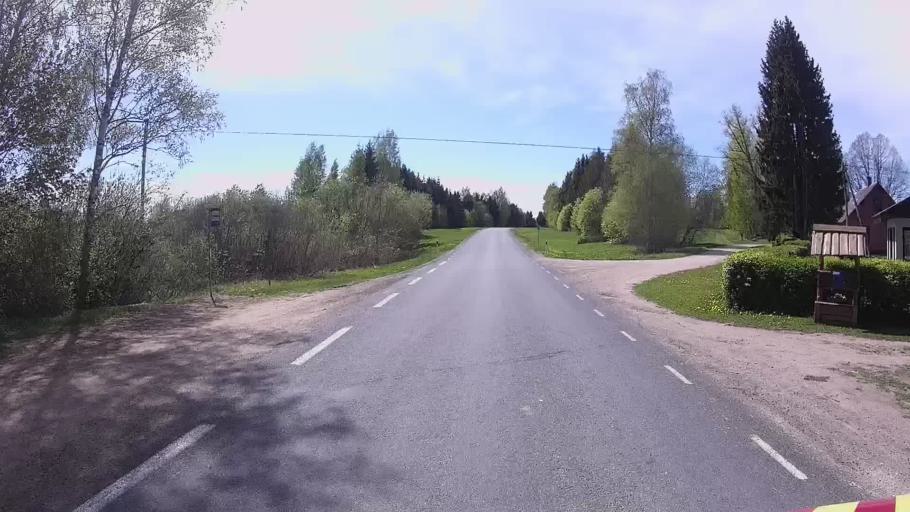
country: LV
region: Apes Novads
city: Ape
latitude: 57.6101
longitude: 26.5723
